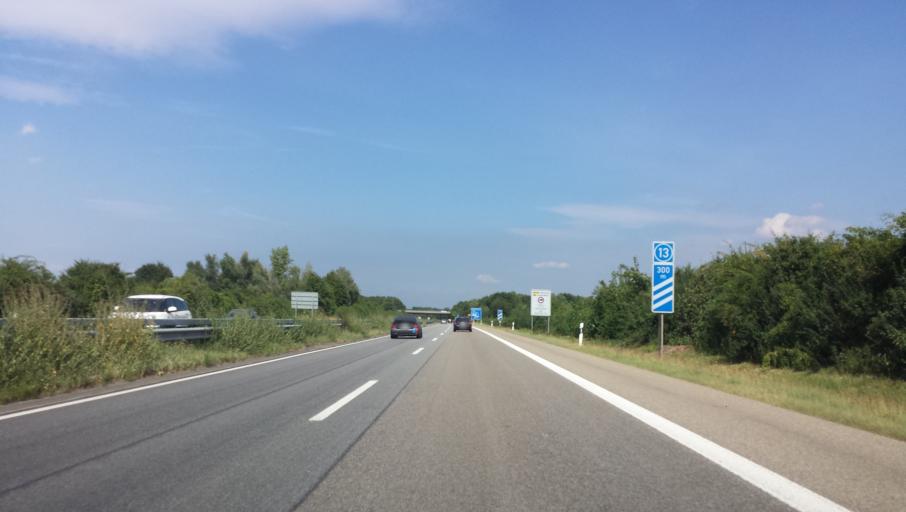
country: DE
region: Rheinland-Pfalz
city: Kirrweiler
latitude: 49.3220
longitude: 8.1731
